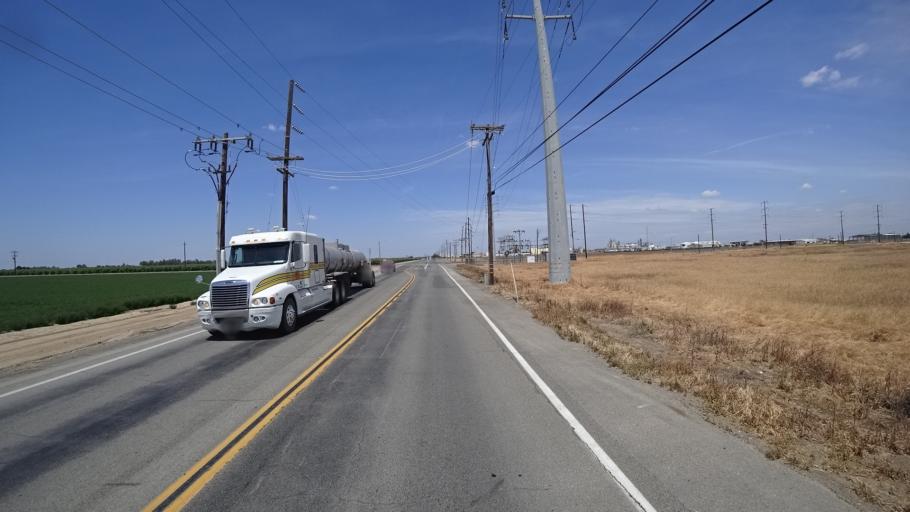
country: US
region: California
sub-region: Kings County
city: Home Garden
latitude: 36.2679
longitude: -119.6549
